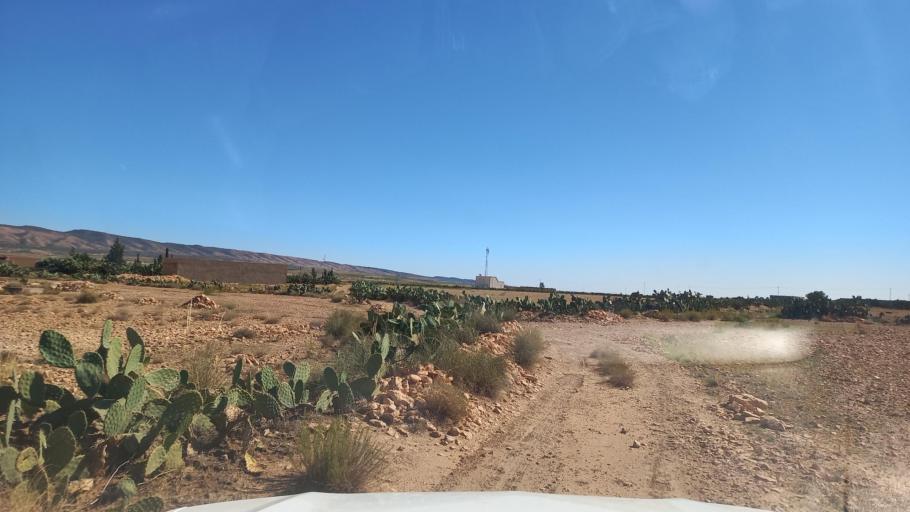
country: TN
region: Al Qasrayn
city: Sbiba
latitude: 35.3848
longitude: 9.0936
